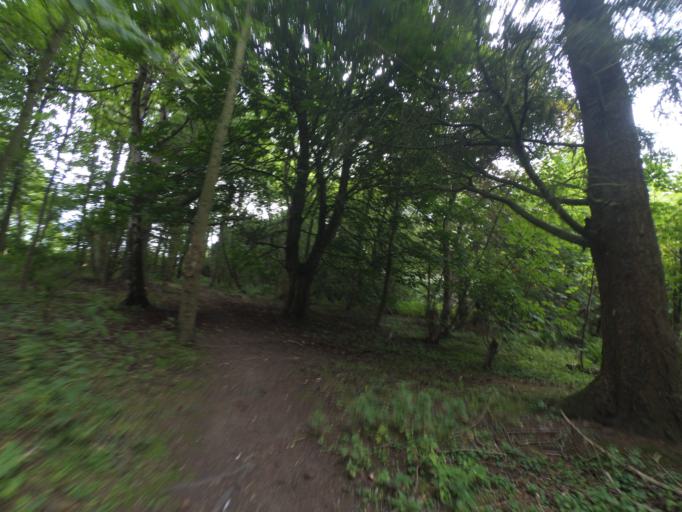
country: GB
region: Scotland
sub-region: Midlothian
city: Bonnyrigg
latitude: 55.9172
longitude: -3.1207
